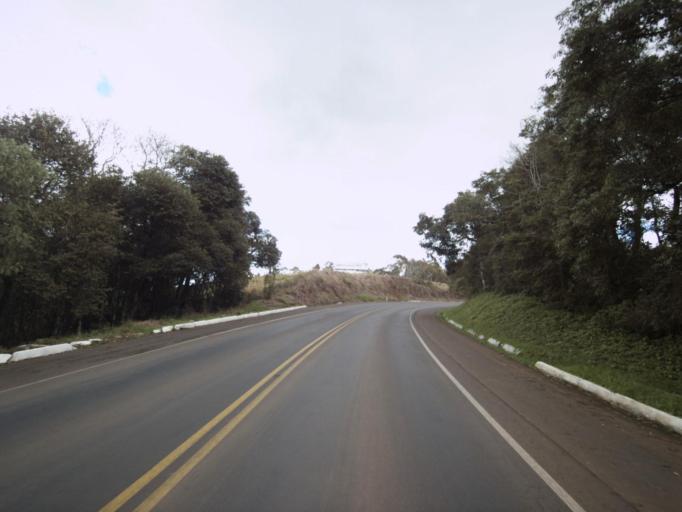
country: BR
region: Santa Catarina
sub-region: Concordia
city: Concordia
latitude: -27.3188
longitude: -51.9859
